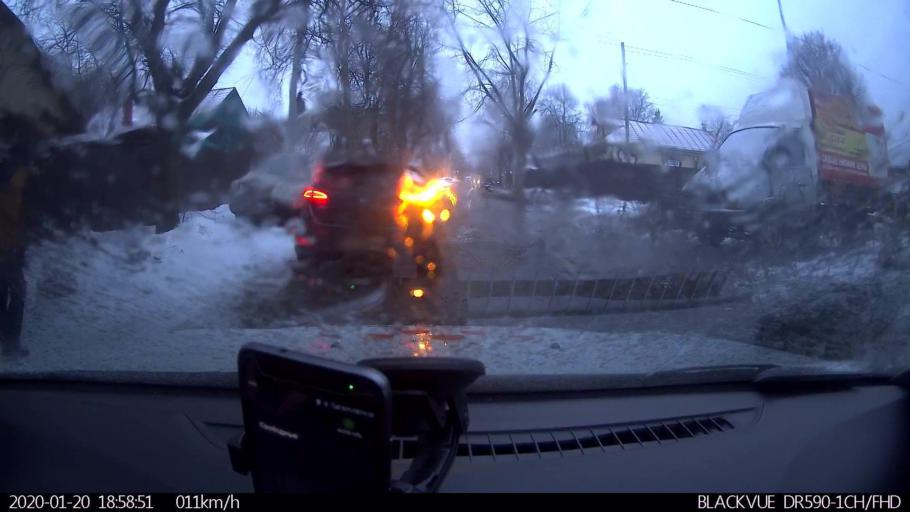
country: RU
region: Nizjnij Novgorod
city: Nizhniy Novgorod
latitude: 56.2962
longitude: 44.0243
